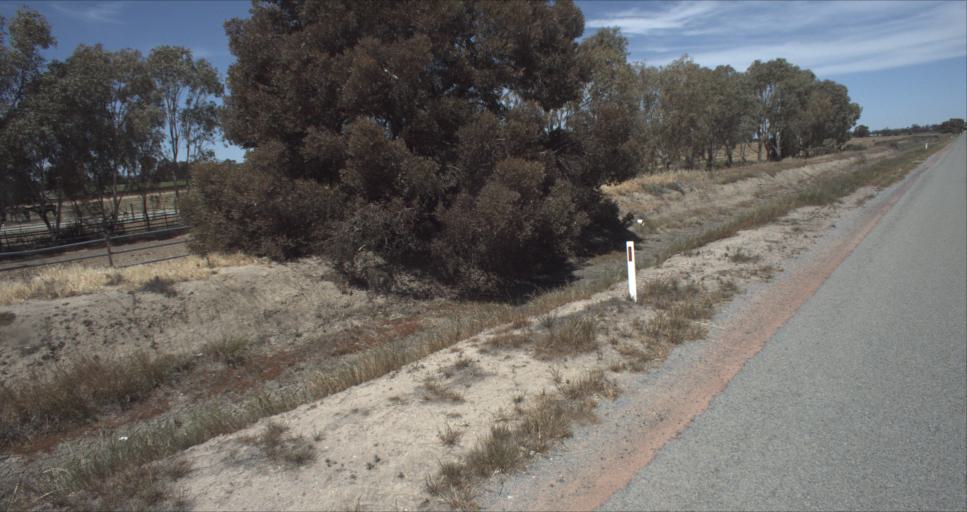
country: AU
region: New South Wales
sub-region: Leeton
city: Leeton
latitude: -34.5970
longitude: 146.4164
